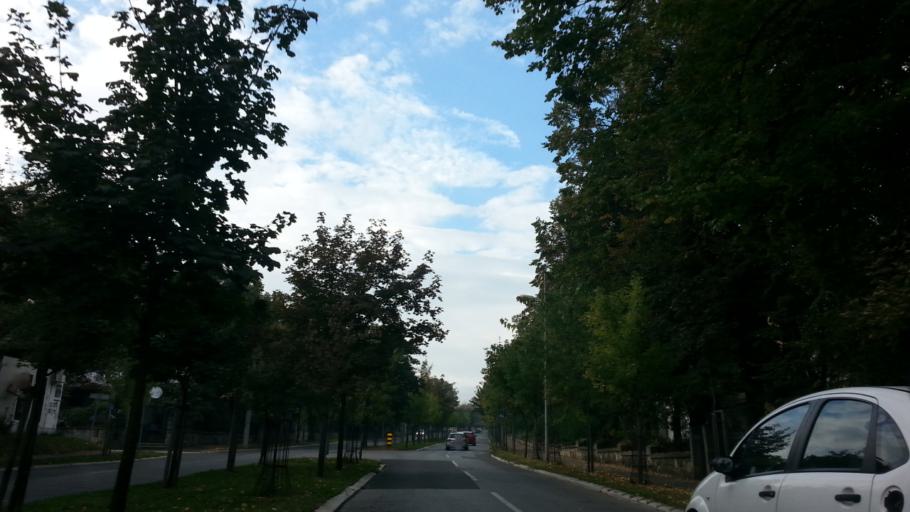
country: RS
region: Central Serbia
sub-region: Belgrade
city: Savski Venac
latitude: 44.7759
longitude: 20.4572
